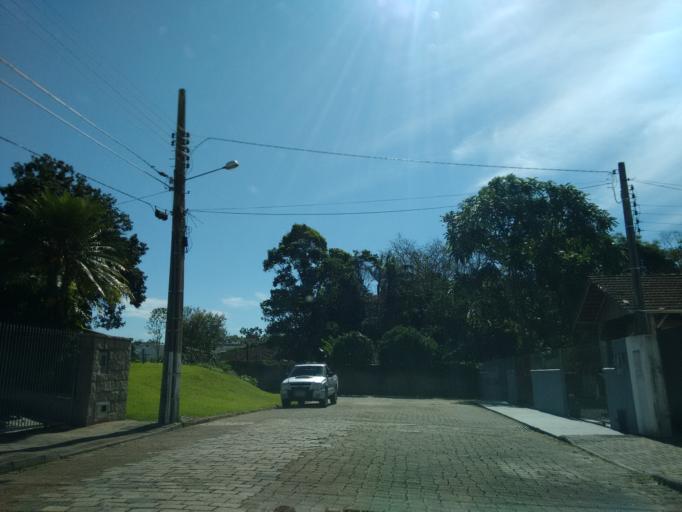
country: BR
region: Santa Catarina
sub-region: Blumenau
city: Blumenau
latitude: -26.8850
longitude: -49.0643
